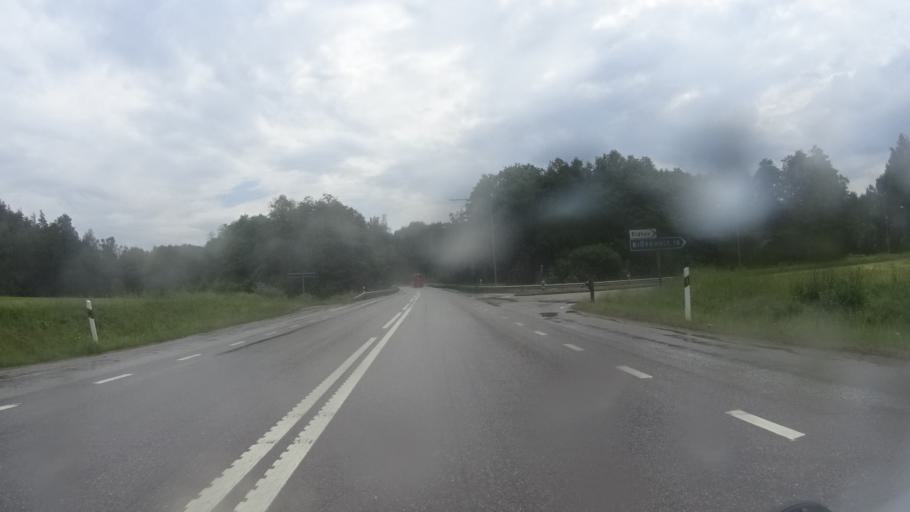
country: SE
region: OEstergoetland
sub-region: Kinda Kommun
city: Kisa
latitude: 57.9766
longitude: 15.6429
